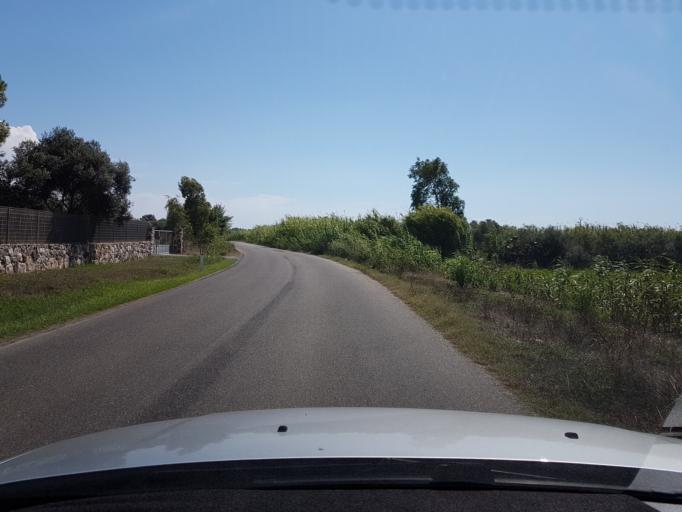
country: IT
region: Sardinia
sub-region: Provincia di Oristano
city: Cabras
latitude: 39.9521
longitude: 8.5308
